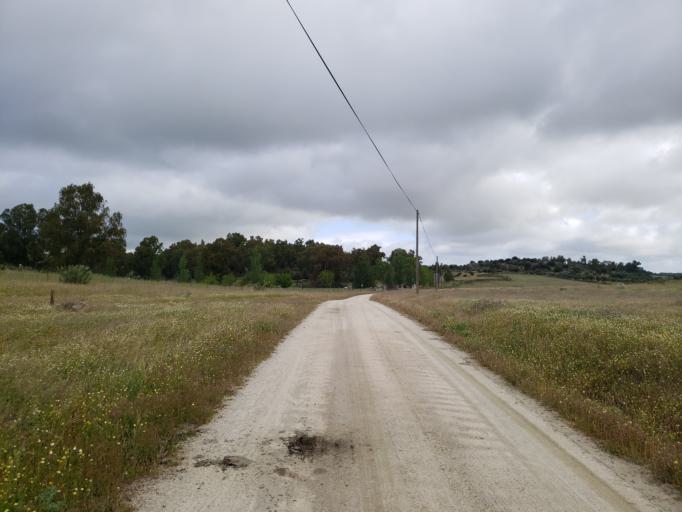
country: ES
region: Extremadura
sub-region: Provincia de Caceres
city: Malpartida de Caceres
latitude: 39.4269
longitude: -6.5043
